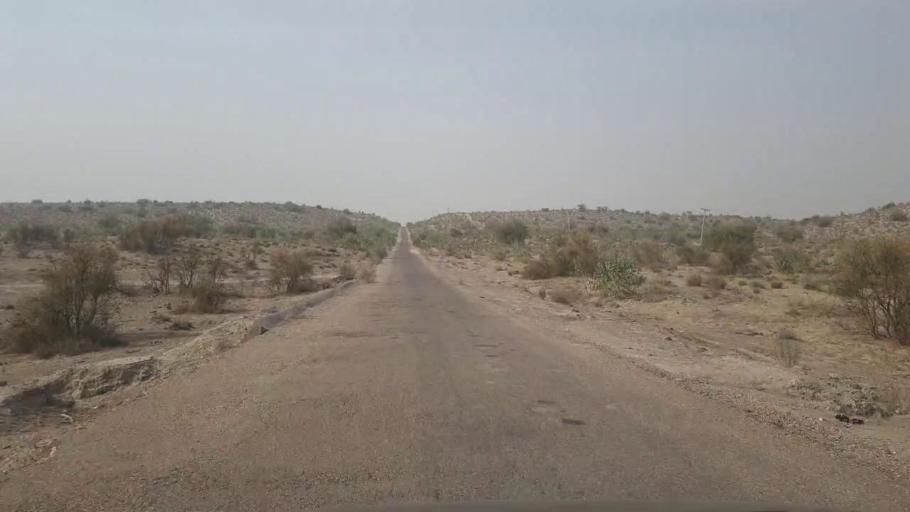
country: PK
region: Sindh
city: Chor
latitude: 25.6086
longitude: 69.9348
